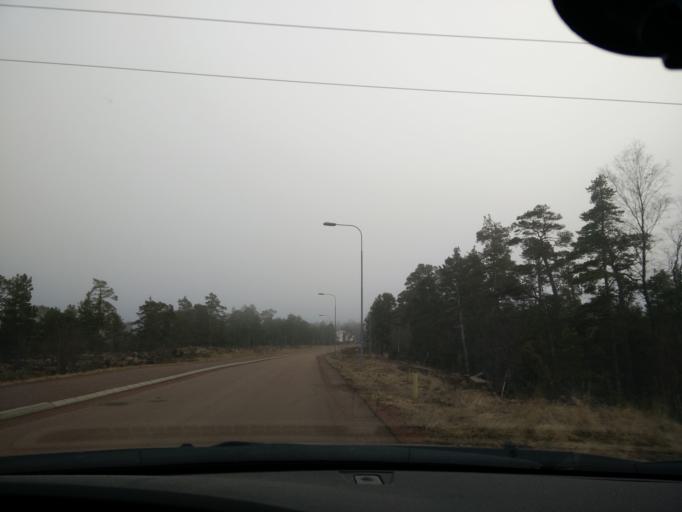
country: AX
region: Alands landsbygd
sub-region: Jomala
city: Jomala
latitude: 60.1277
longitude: 19.9287
